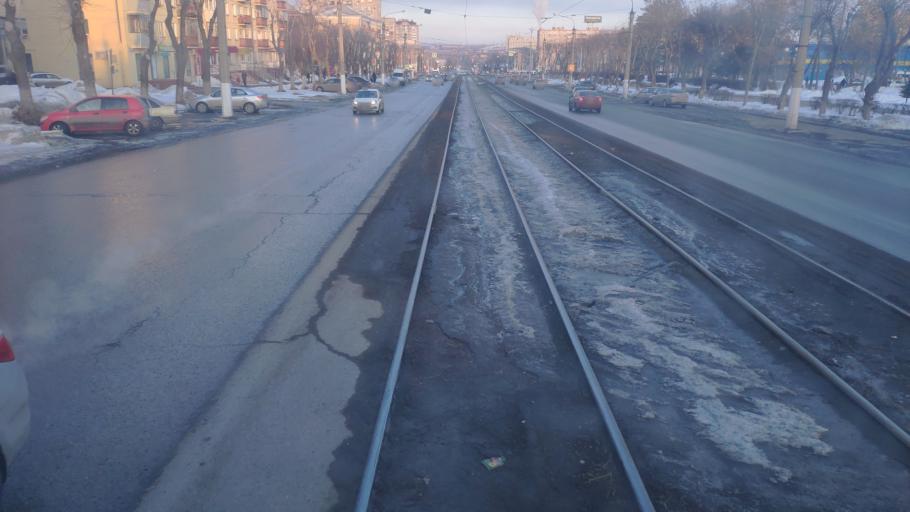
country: RU
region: Chelyabinsk
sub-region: Gorod Magnitogorsk
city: Magnitogorsk
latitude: 53.3981
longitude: 58.9723
